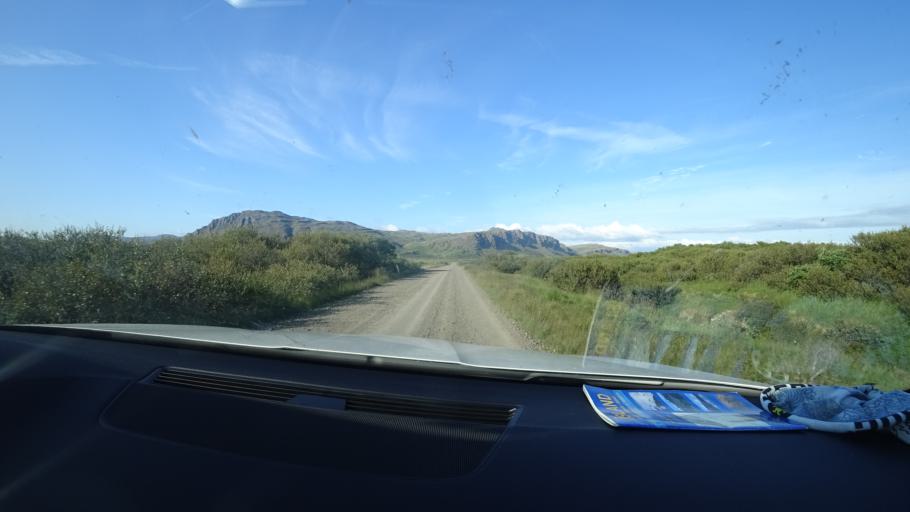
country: IS
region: West
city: Borgarnes
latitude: 64.6832
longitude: -21.9493
